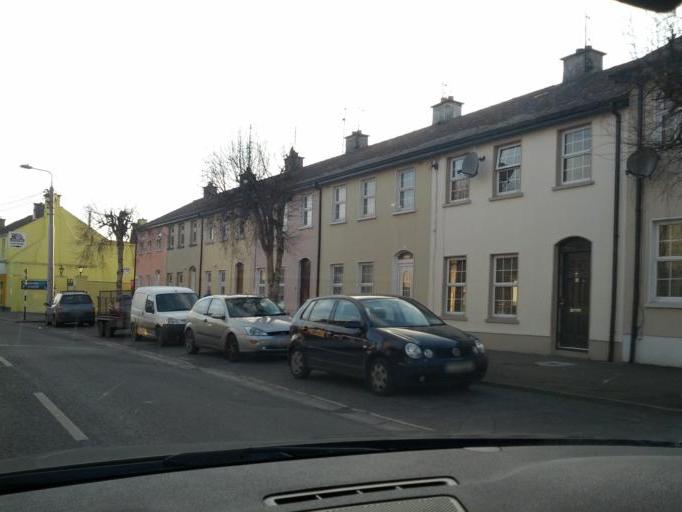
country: IE
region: Munster
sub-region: North Tipperary
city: Nenagh
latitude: 52.8618
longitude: -8.2017
